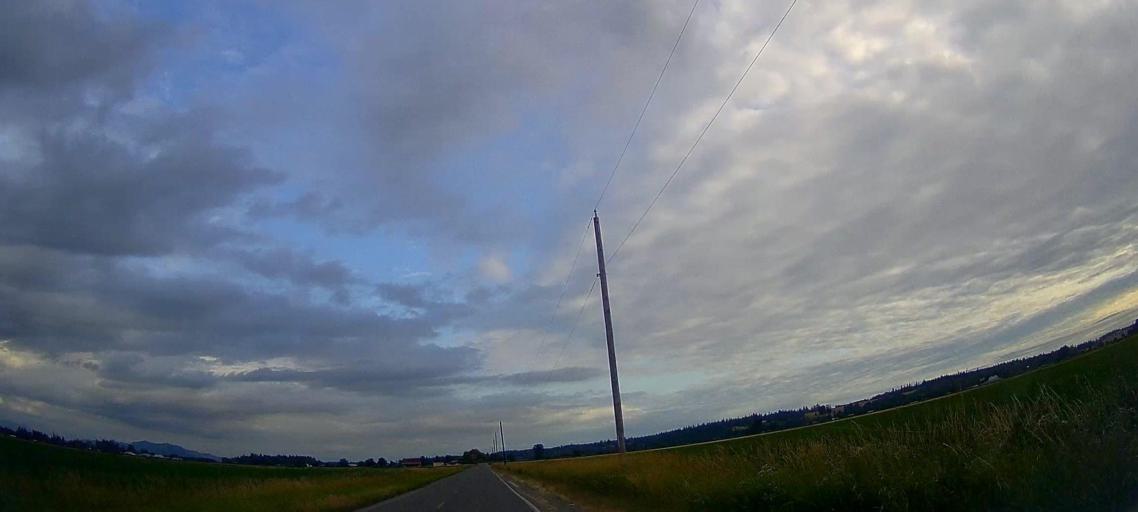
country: US
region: Washington
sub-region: Skagit County
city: Burlington
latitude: 48.5284
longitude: -122.4114
